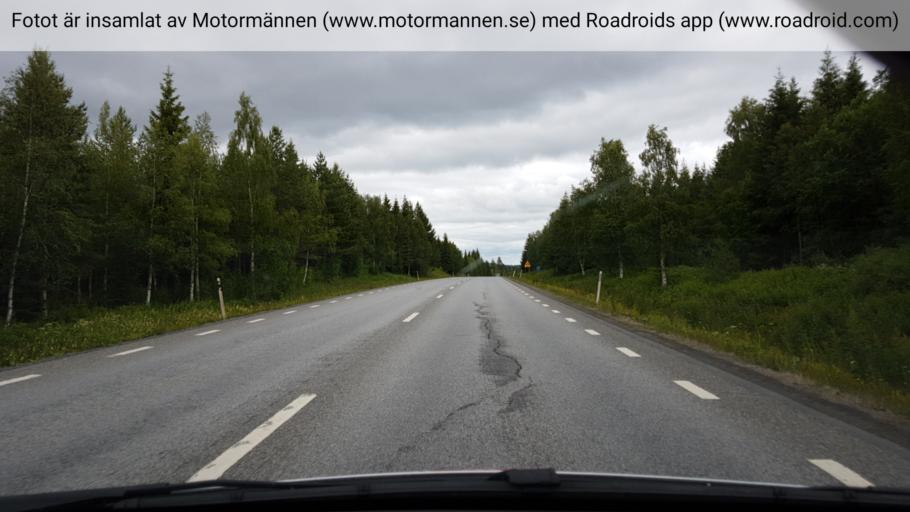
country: SE
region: Jaemtland
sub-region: Krokoms Kommun
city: Valla
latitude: 63.3139
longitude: 13.9342
